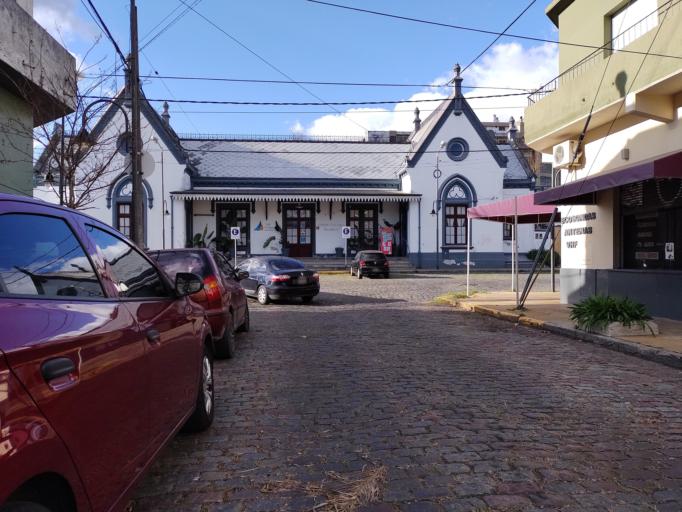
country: AR
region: Buenos Aires
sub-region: Partido de Tigre
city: Tigre
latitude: -34.4379
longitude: -58.5544
